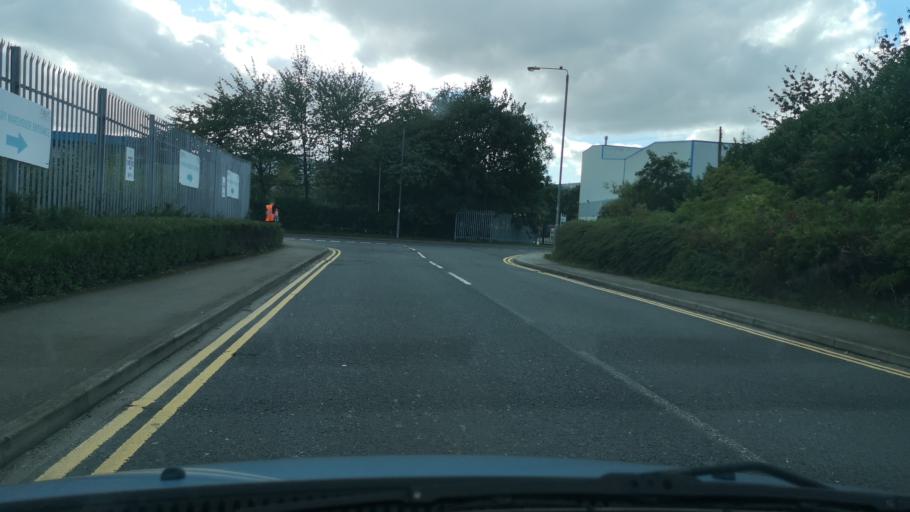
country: GB
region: England
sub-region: City and Borough of Wakefield
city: South Elmsall
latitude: 53.6036
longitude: -1.2742
